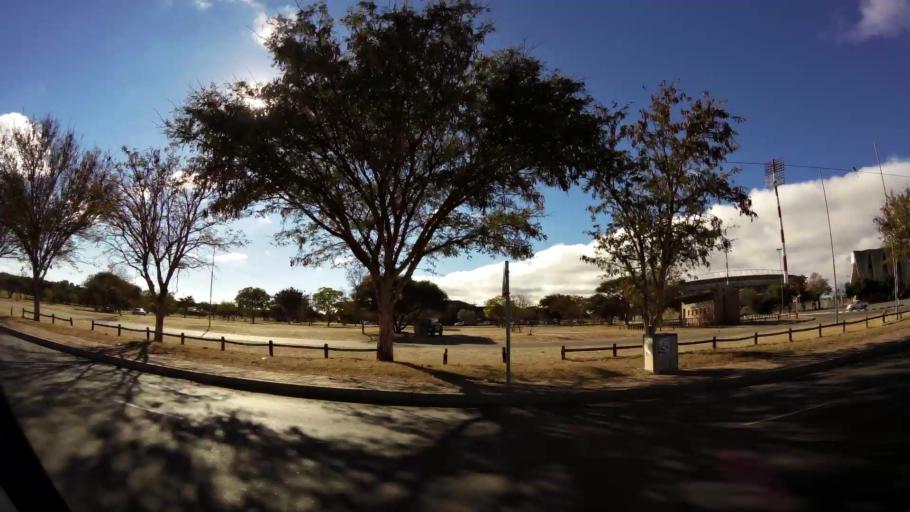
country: ZA
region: Limpopo
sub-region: Capricorn District Municipality
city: Polokwane
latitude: -23.9228
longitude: 29.4631
